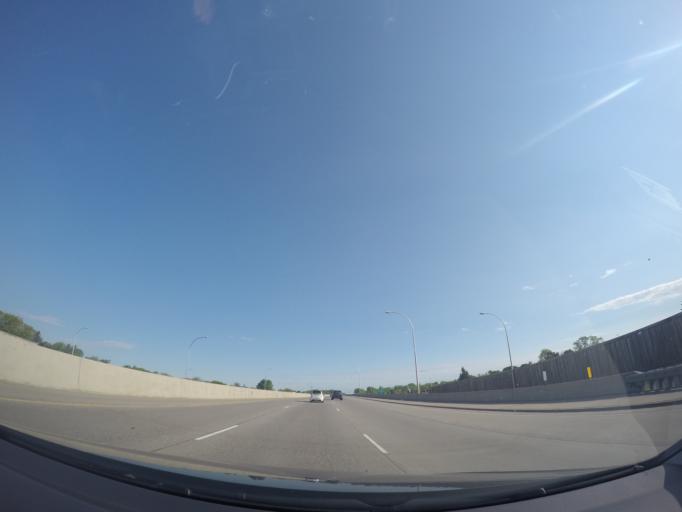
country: US
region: Minnesota
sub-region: Hennepin County
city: Golden Valley
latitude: 44.9821
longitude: -93.3486
